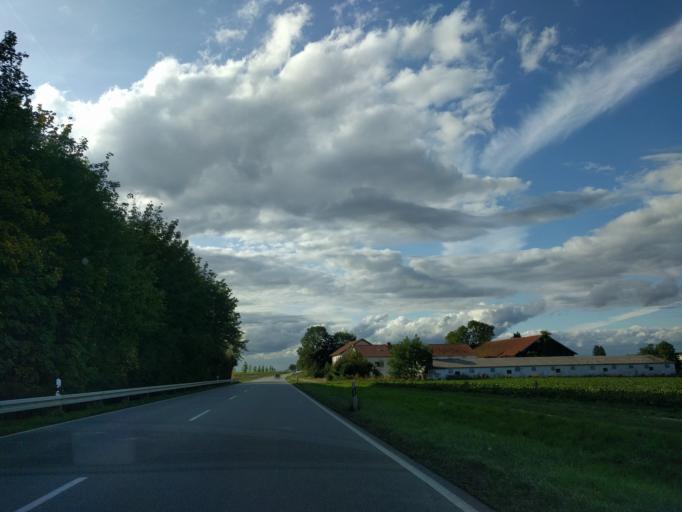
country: DE
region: Bavaria
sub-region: Lower Bavaria
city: Stephansposching
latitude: 48.7982
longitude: 12.8124
